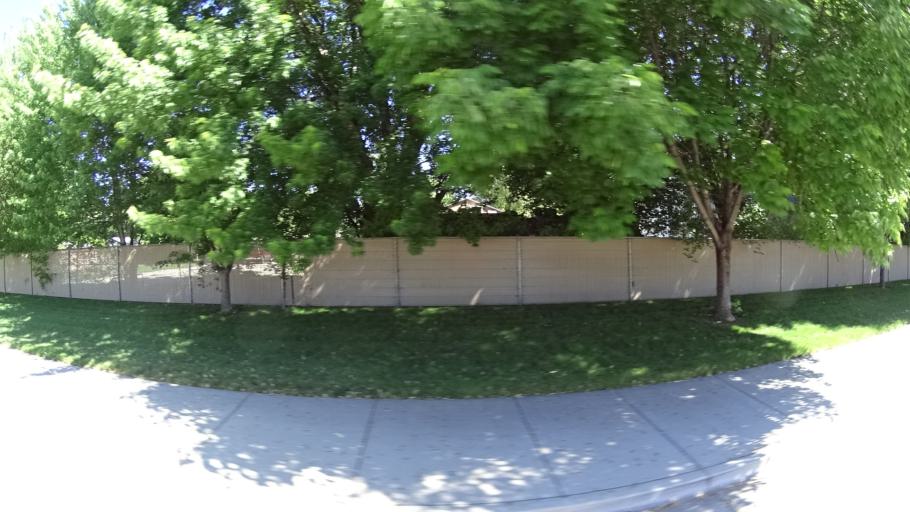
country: US
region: Idaho
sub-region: Ada County
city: Meridian
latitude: 43.6410
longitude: -116.3712
